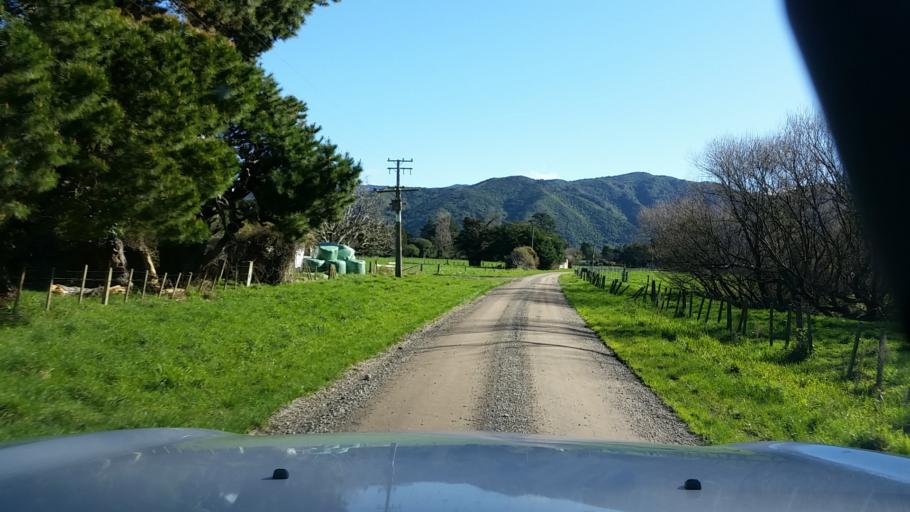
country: NZ
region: Wellington
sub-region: Masterton District
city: Masterton
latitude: -41.0579
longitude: 175.4152
